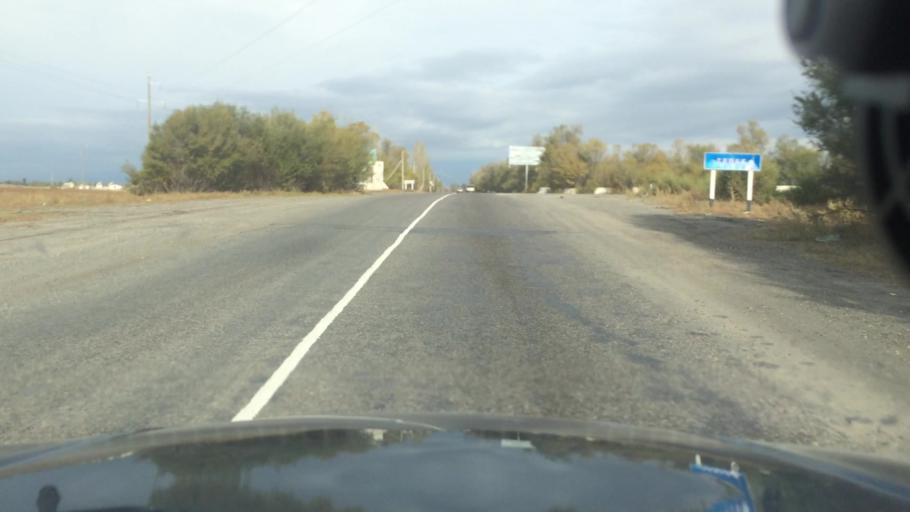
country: KG
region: Ysyk-Koel
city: Karakol
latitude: 42.5984
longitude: 78.3748
